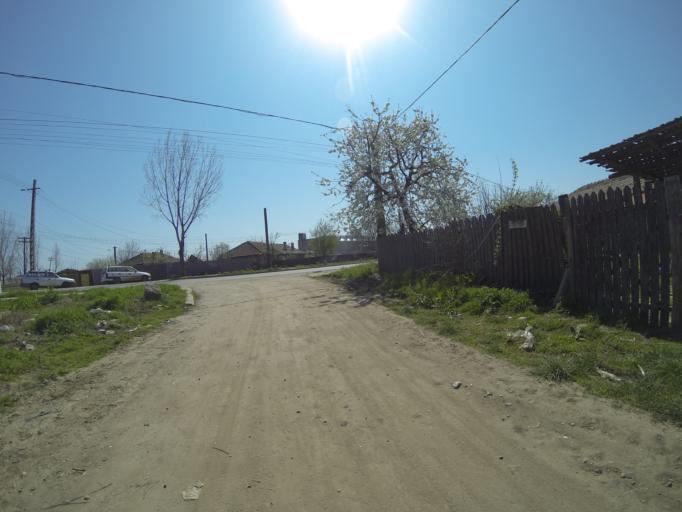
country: RO
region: Dolj
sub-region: Comuna Segarcea
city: Segarcea
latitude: 44.0891
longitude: 23.7298
